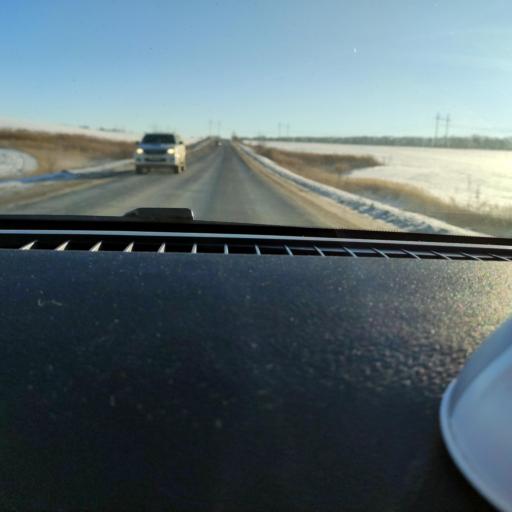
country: RU
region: Samara
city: Kinel'
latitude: 53.1476
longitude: 50.5146
